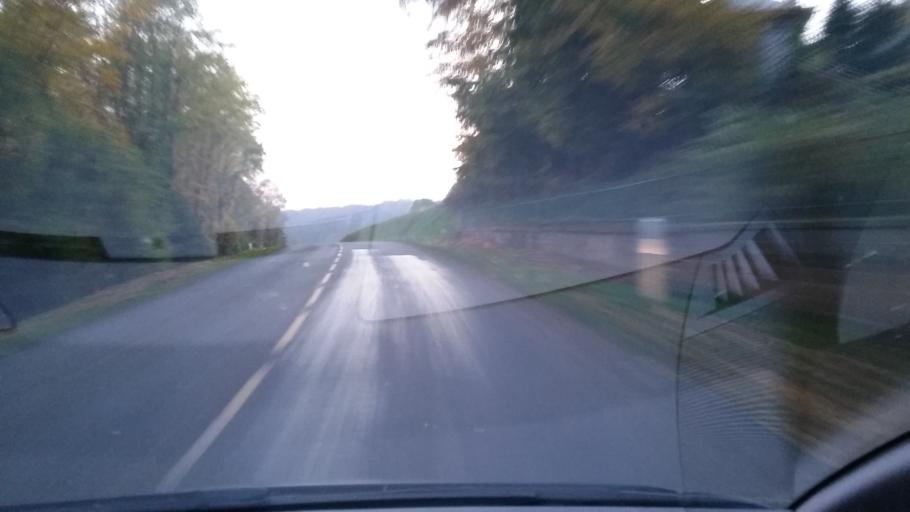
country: FR
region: Lorraine
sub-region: Departement de la Moselle
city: Soucht
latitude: 48.8655
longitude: 7.3122
